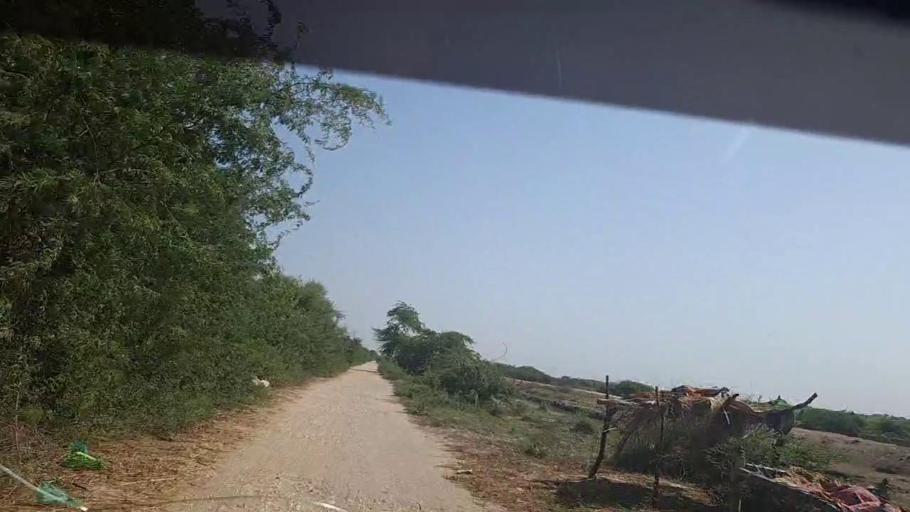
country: PK
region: Sindh
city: Rajo Khanani
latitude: 24.9773
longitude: 68.8672
